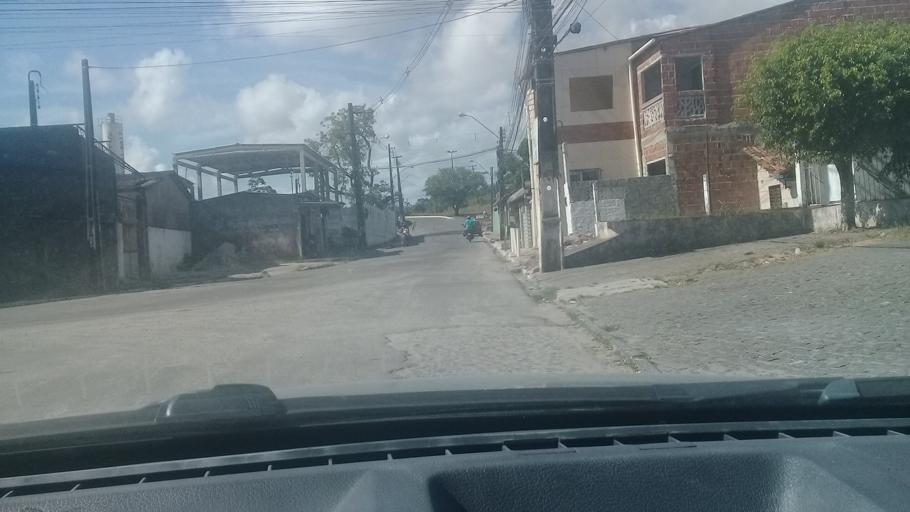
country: BR
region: Pernambuco
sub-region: Jaboatao Dos Guararapes
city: Jaboatao dos Guararapes
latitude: -8.0922
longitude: -35.0225
